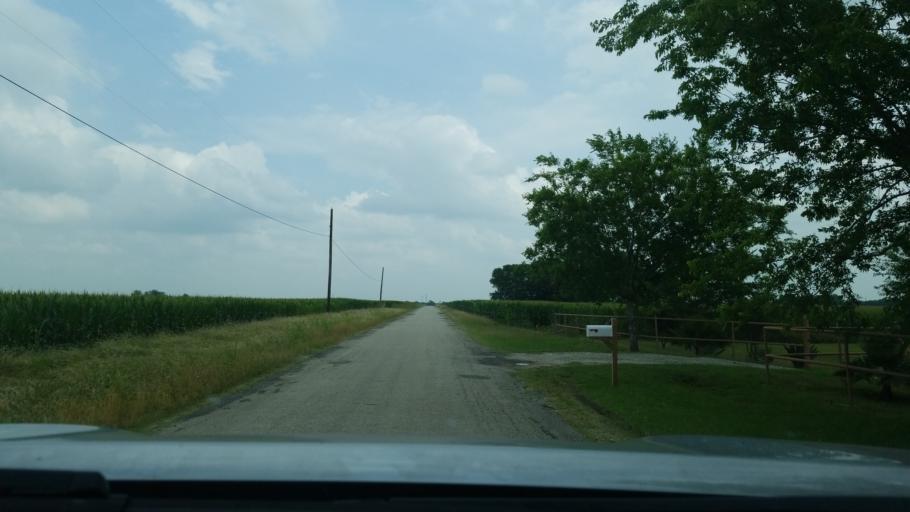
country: US
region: Texas
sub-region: Guadalupe County
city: Geronimo
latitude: 29.6802
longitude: -98.0096
